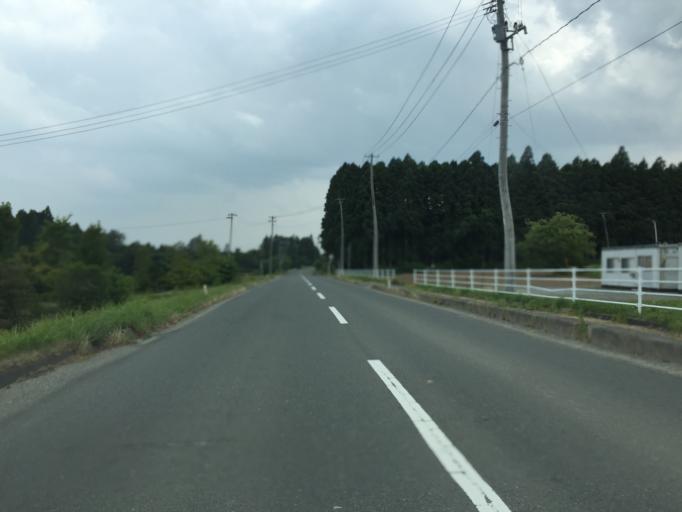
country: JP
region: Miyagi
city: Marumori
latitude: 37.8703
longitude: 140.8873
